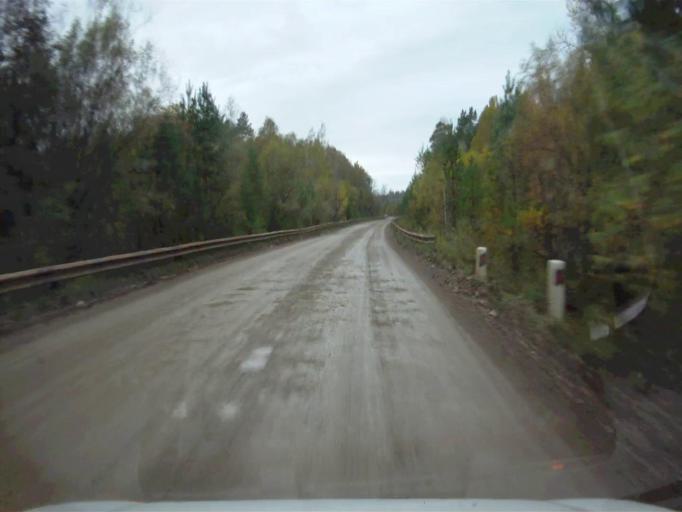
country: RU
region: Chelyabinsk
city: Nyazepetrovsk
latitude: 56.1284
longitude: 59.3300
